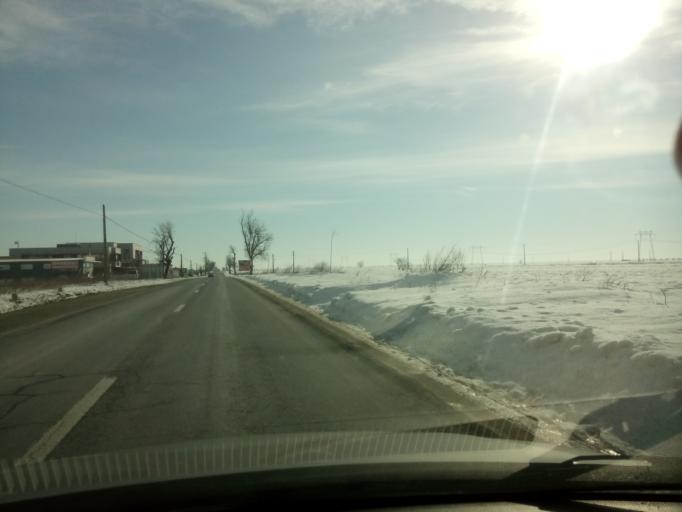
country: RO
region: Calarasi
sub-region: Comuna Frumusani
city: Frumusani
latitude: 44.2753
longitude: 26.3386
